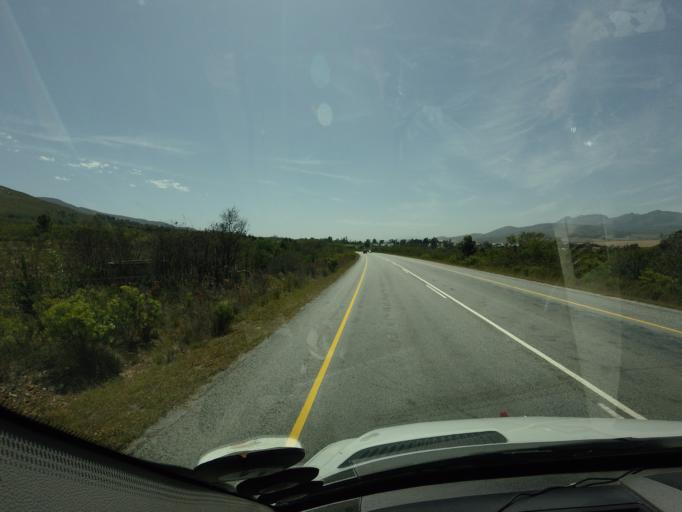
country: ZA
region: Western Cape
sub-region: Overberg District Municipality
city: Hermanus
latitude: -34.3183
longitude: 19.1188
